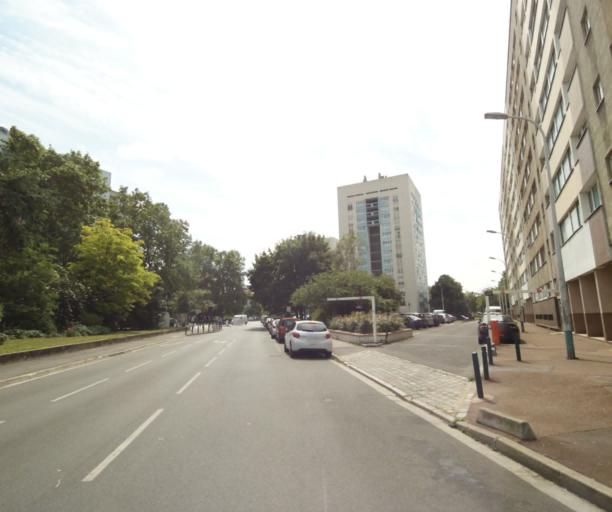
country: FR
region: Ile-de-France
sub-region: Departement des Hauts-de-Seine
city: Asnieres-sur-Seine
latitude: 48.9231
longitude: 2.2873
